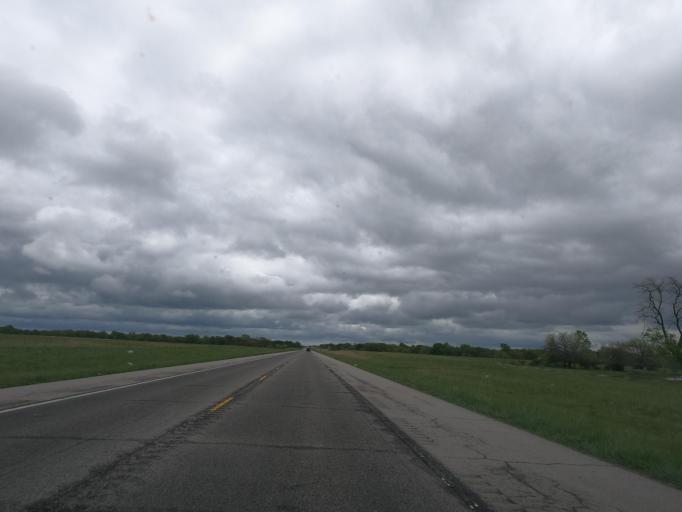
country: US
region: Kansas
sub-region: Labette County
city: Parsons
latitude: 37.3429
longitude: -95.3932
